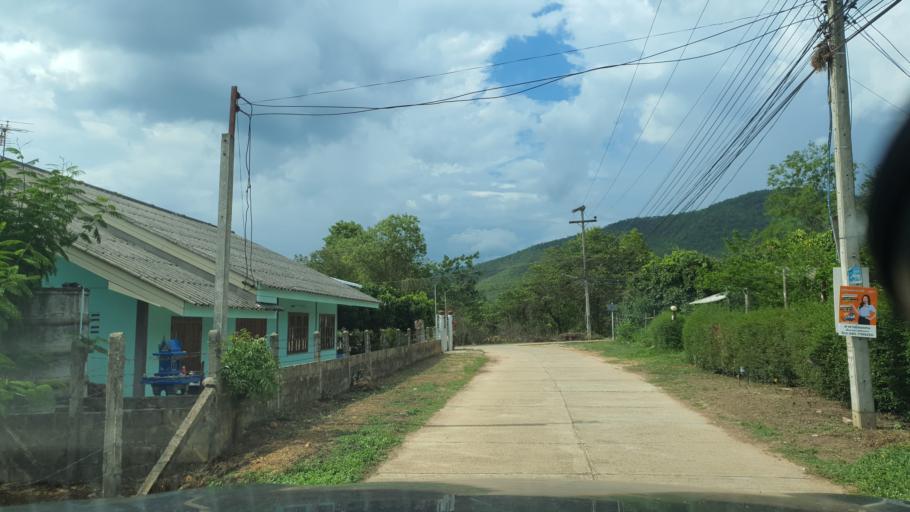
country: TH
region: Chiang Mai
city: Mae Taeng
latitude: 19.1413
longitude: 99.0374
